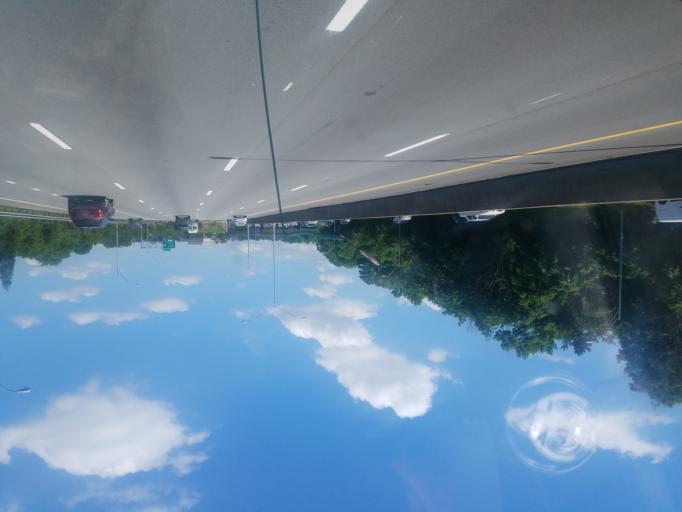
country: US
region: Ohio
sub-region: Hamilton County
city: Norwood
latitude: 39.1474
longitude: -84.4523
